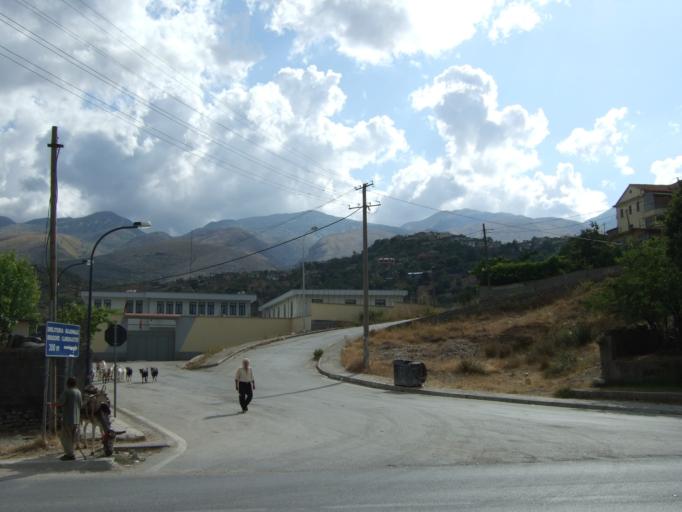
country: AL
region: Gjirokaster
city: Gjirokaster
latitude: 40.0749
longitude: 20.1543
